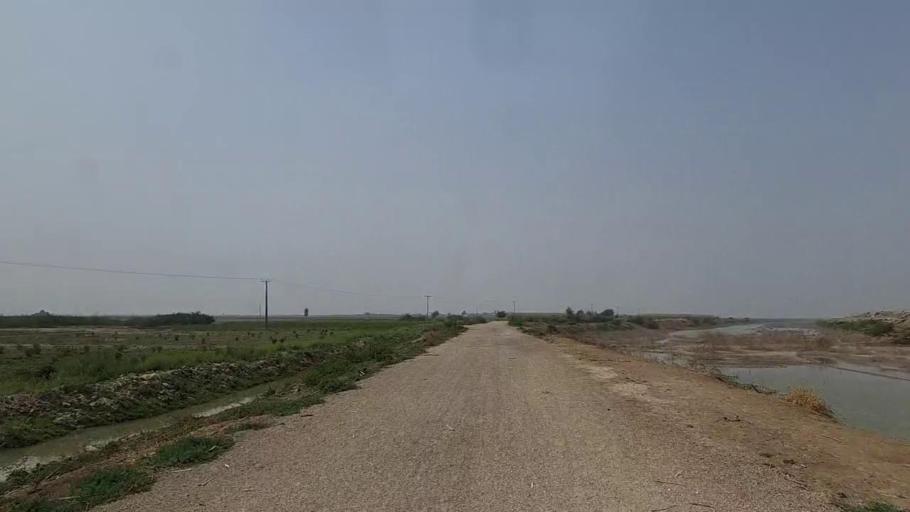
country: PK
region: Sindh
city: Naukot
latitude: 24.7957
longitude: 69.3447
